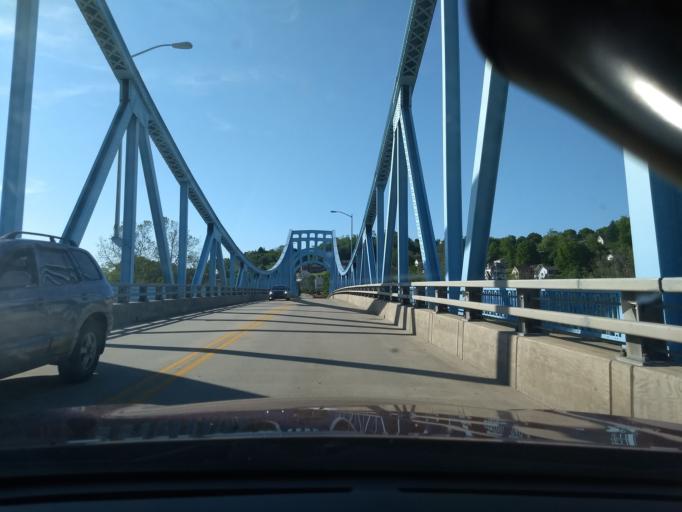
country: US
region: Pennsylvania
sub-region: Allegheny County
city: Versailles
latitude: 40.3125
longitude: -79.8279
